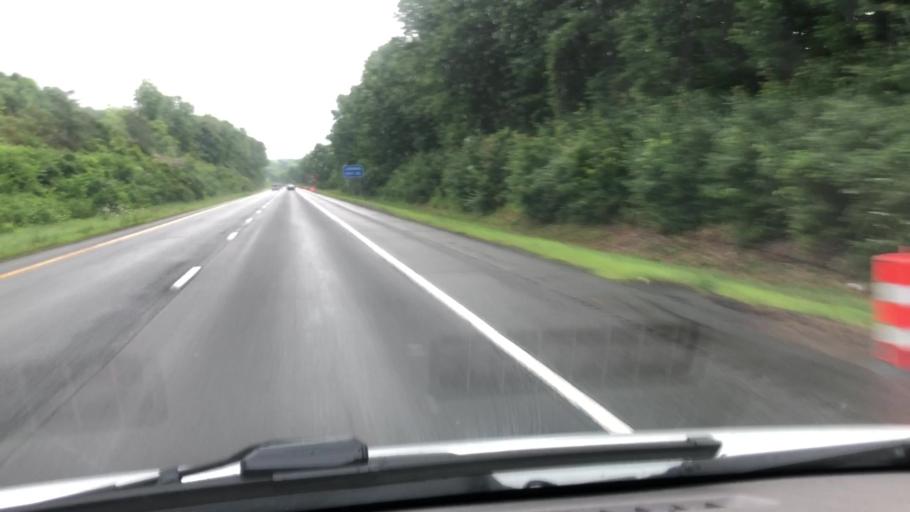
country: US
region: Massachusetts
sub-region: Franklin County
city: Greenfield
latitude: 42.5537
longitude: -72.6204
